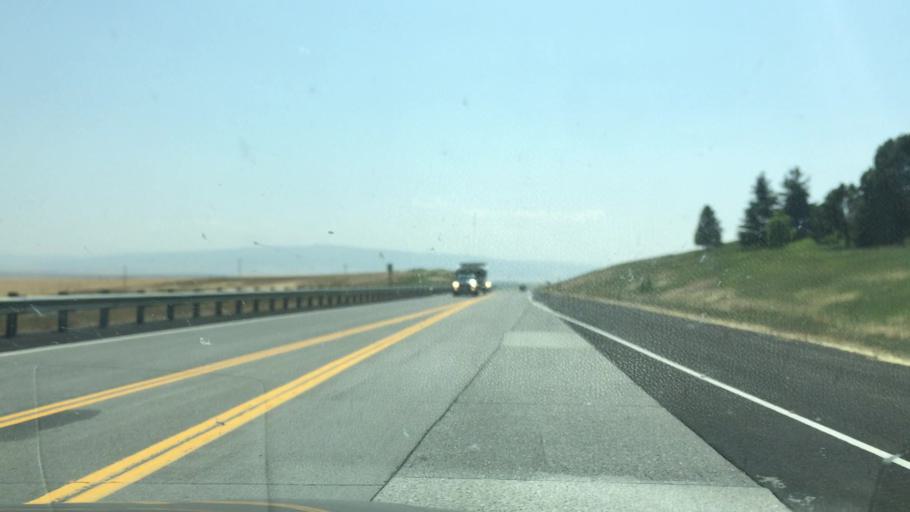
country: US
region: Idaho
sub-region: Lewis County
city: Nezperce
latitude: 46.0430
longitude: -116.3420
